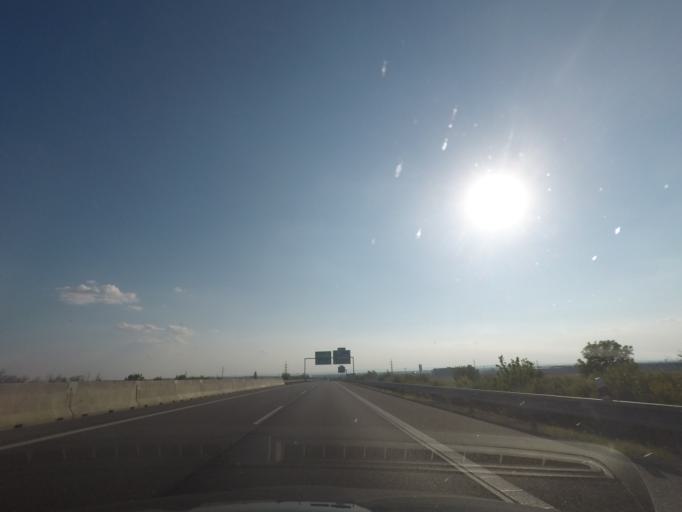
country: CZ
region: Olomoucky
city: Velky Tynec
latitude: 49.5634
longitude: 17.3270
